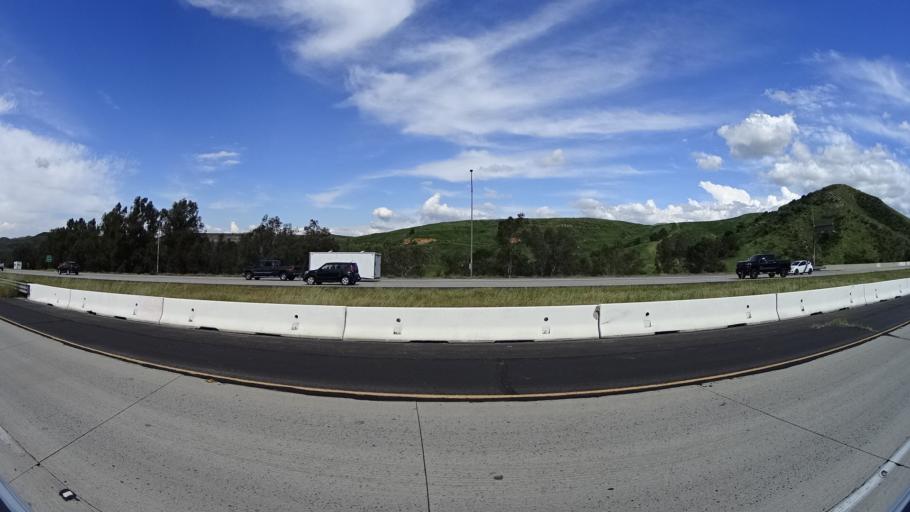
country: US
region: California
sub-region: Riverside County
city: El Cerrito
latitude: 33.7741
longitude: -117.4860
